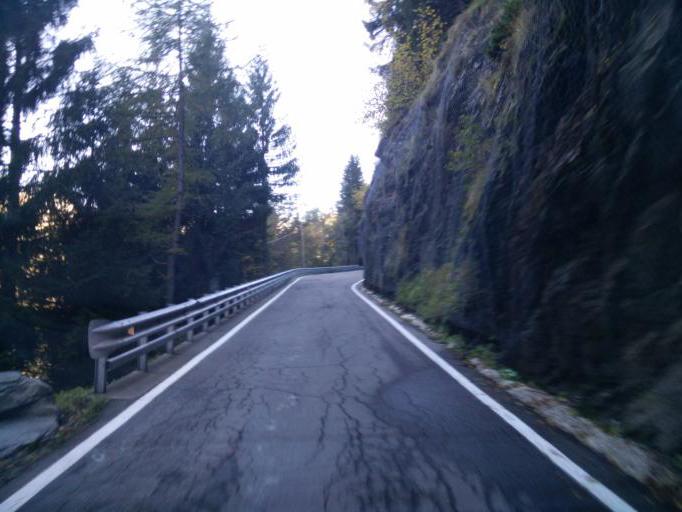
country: IT
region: Trentino-Alto Adige
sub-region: Bolzano
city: Moso in Passiria
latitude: 46.8407
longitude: 11.1678
